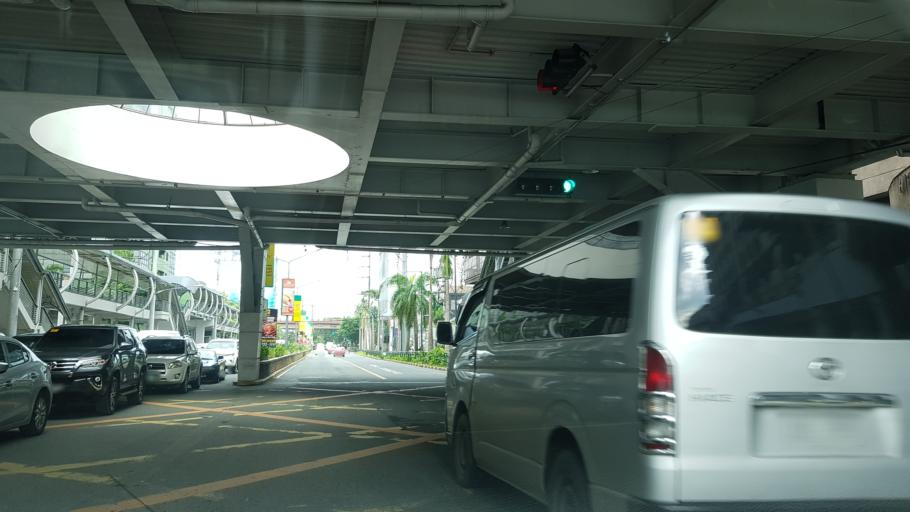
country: PH
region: Metro Manila
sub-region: Pasig
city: Pasig City
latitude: 14.5843
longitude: 121.0615
